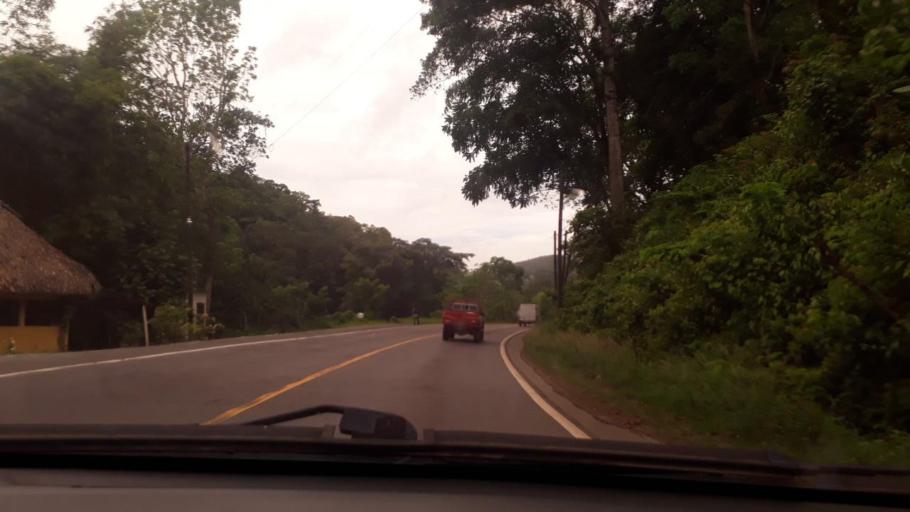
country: GT
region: Izabal
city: Morales
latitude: 15.5359
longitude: -88.7612
